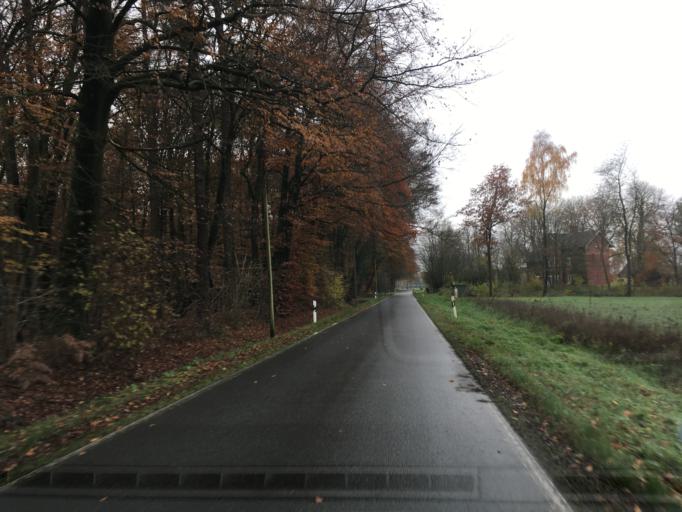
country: DE
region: North Rhine-Westphalia
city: Stadtlohn
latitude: 52.0192
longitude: 6.9783
